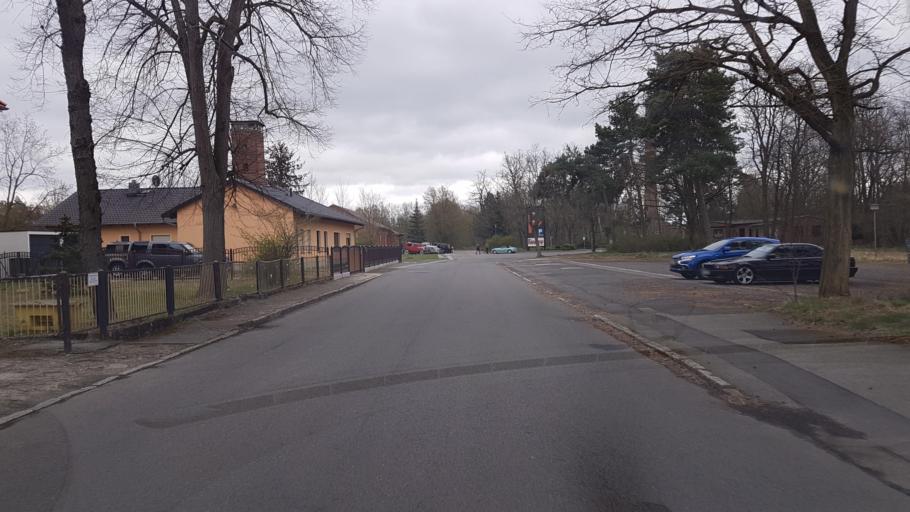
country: DE
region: Saxony
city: Lohsa
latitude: 51.4015
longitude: 14.3265
